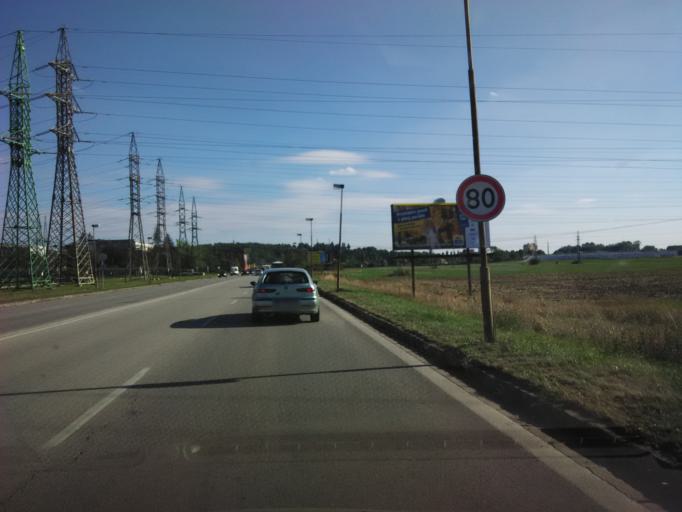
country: SK
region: Nitriansky
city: Levice
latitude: 48.2341
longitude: 18.5992
